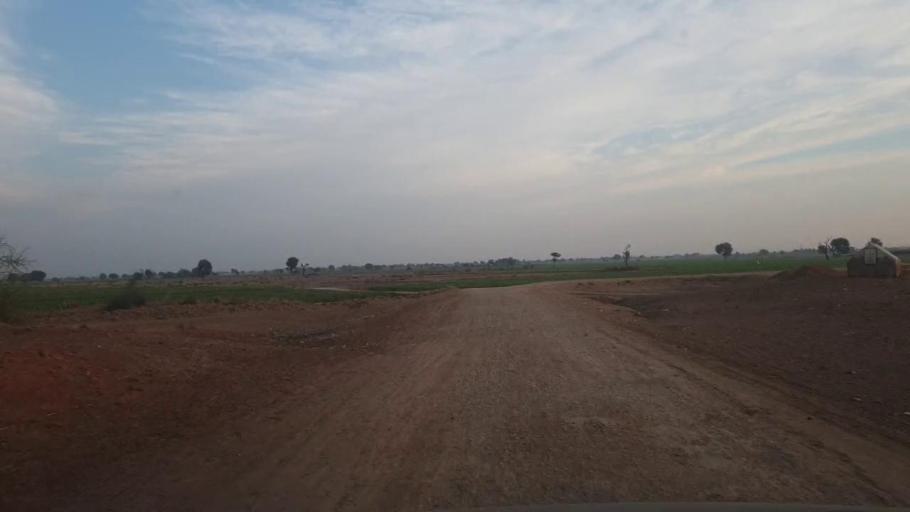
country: PK
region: Sindh
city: Shahpur Chakar
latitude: 26.0593
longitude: 68.5297
